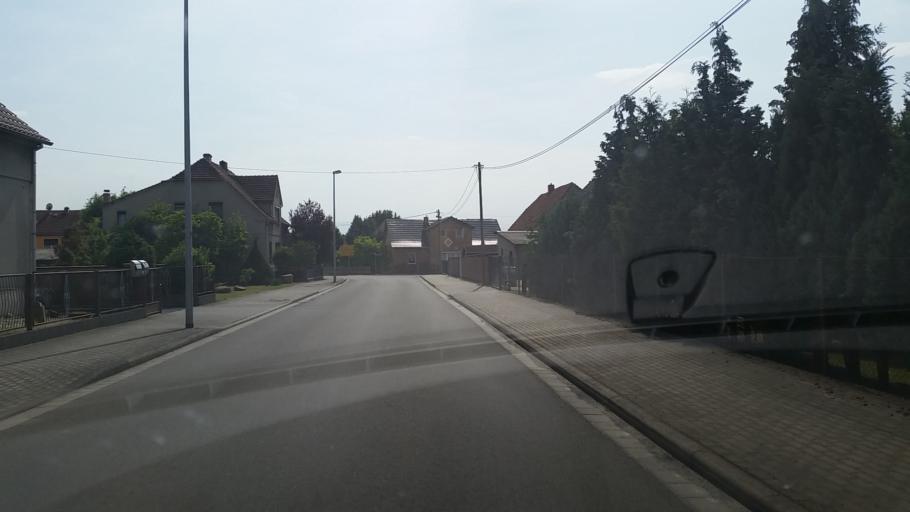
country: DE
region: Brandenburg
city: Hermsdorf
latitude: 51.4052
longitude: 13.8967
